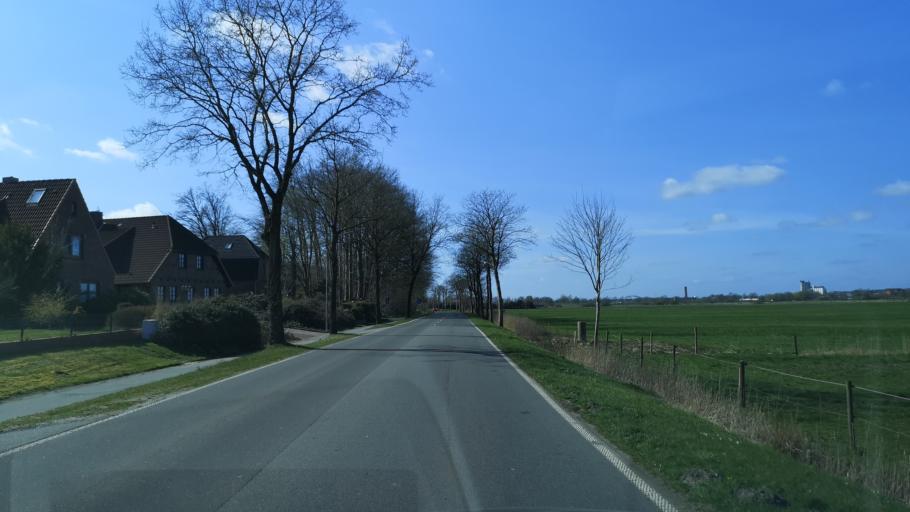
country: DE
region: Schleswig-Holstein
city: Munsterdorf
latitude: 53.9049
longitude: 9.5299
